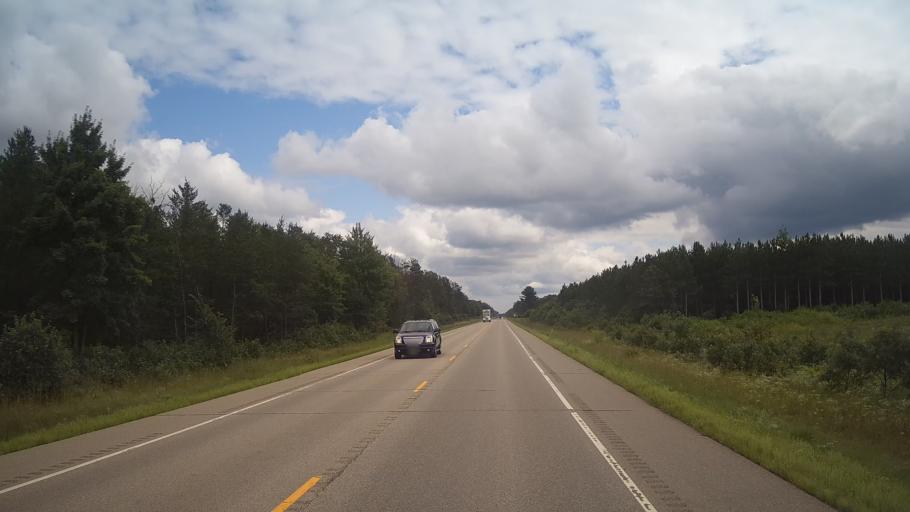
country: US
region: Wisconsin
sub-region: Adams County
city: Friendship
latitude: 44.0251
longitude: -89.7544
